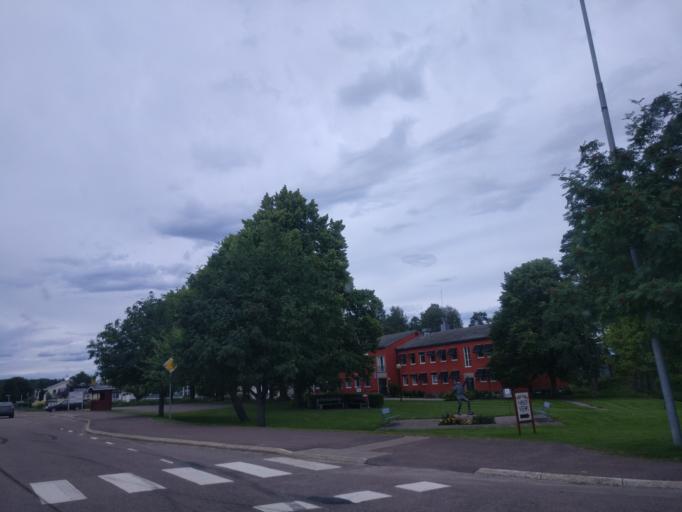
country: SE
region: Vaermland
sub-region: Hagfors Kommun
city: Ekshaerad
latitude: 60.1728
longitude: 13.4965
